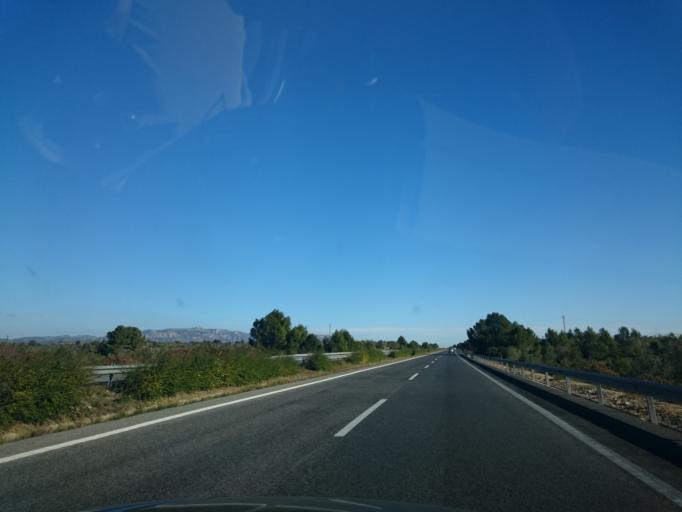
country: ES
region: Catalonia
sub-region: Provincia de Tarragona
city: l'Ametlla de Mar
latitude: 40.8604
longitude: 0.7696
